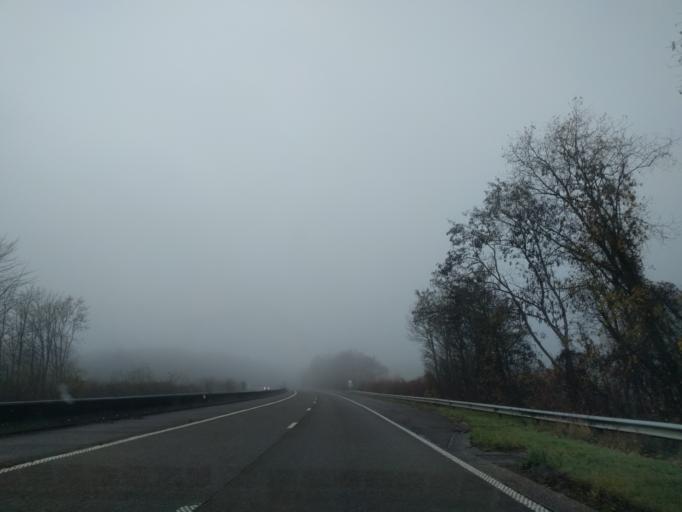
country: BE
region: Wallonia
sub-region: Province de Namur
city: Dinant
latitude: 50.2429
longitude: 4.9125
